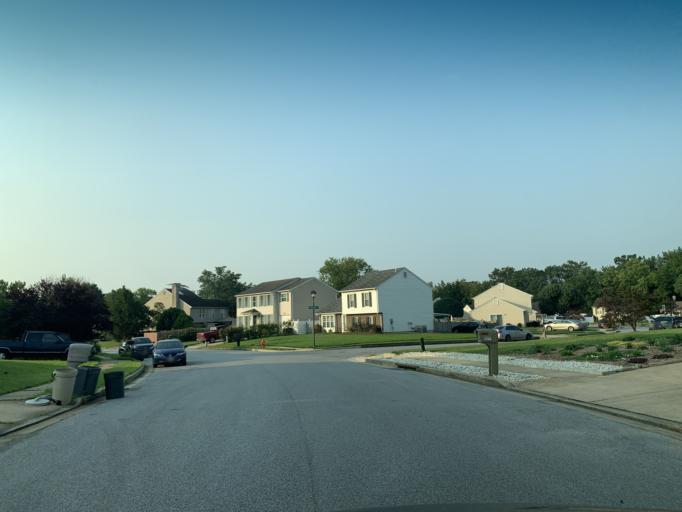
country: US
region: Maryland
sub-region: Baltimore County
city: Bowleys Quarters
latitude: 39.3643
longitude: -76.3630
